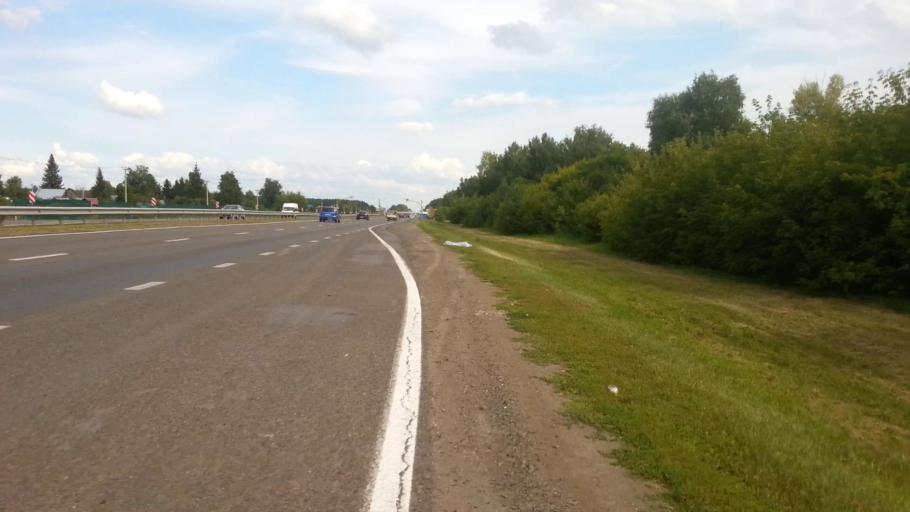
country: RU
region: Altai Krai
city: Nauchnyy Gorodok
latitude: 53.3546
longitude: 83.5367
